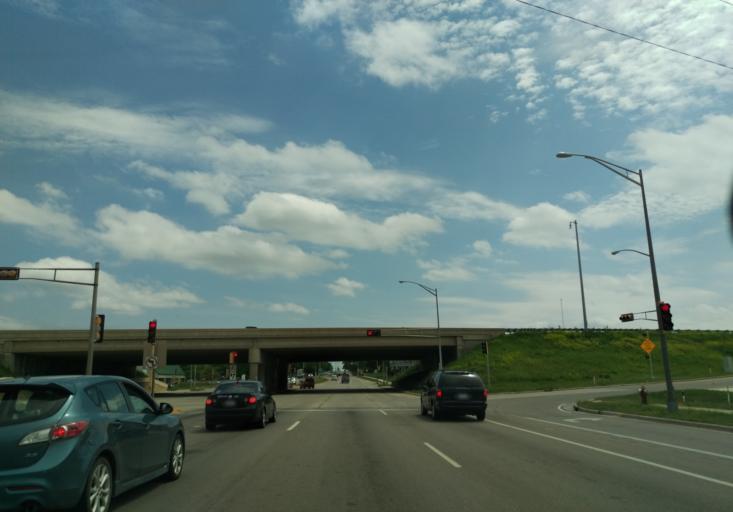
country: US
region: Wisconsin
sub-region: Dane County
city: Middleton
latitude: 43.0604
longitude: -89.5235
